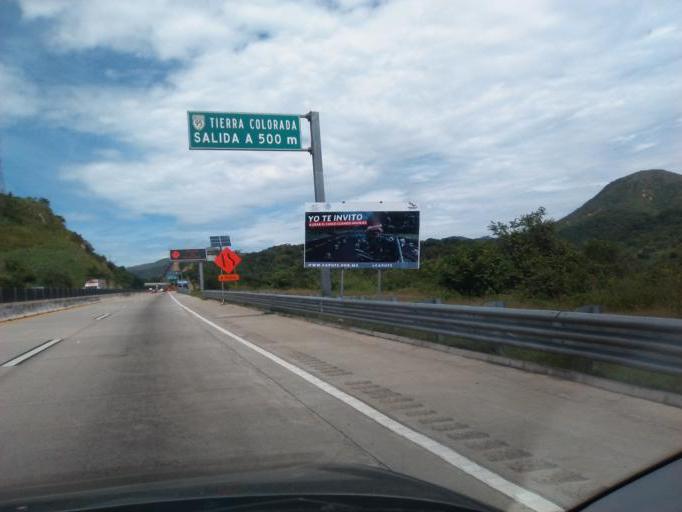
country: MX
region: Guerrero
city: Tierra Colorada
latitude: 17.1718
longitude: -99.5541
